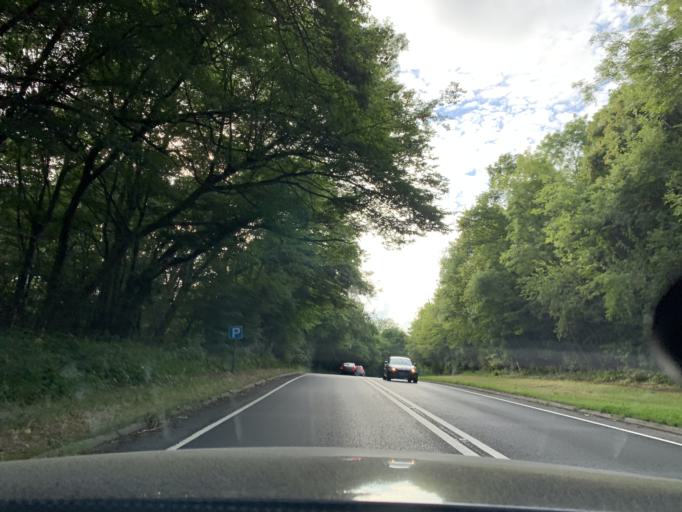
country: GB
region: England
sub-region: East Sussex
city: Robertsbridge
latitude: 51.0400
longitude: 0.4516
